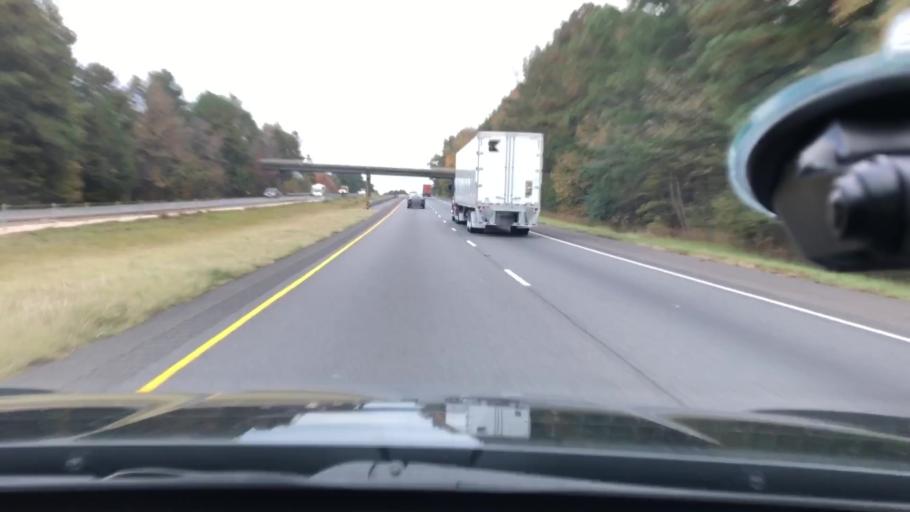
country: US
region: Arkansas
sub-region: Clark County
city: Arkadelphia
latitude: 34.2336
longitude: -93.0089
